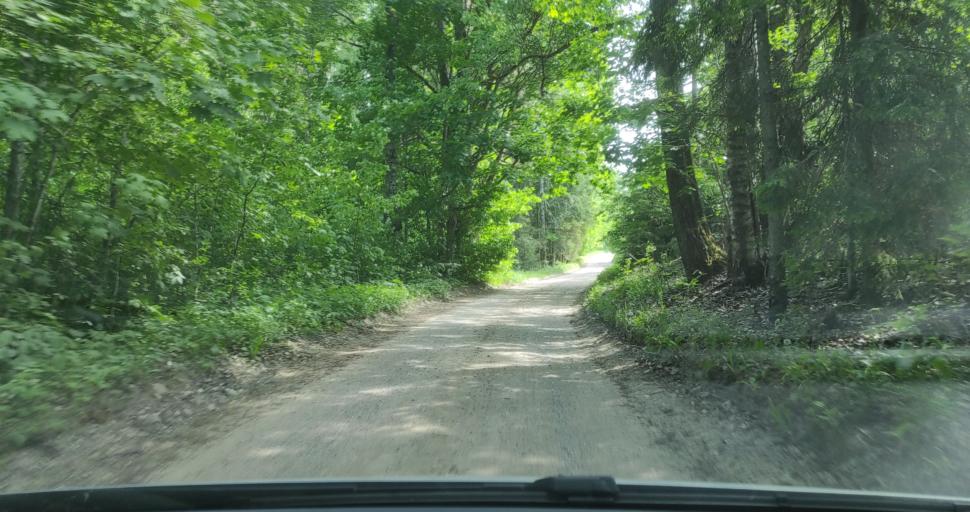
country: LV
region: Kuldigas Rajons
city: Kuldiga
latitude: 56.8635
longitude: 21.9079
